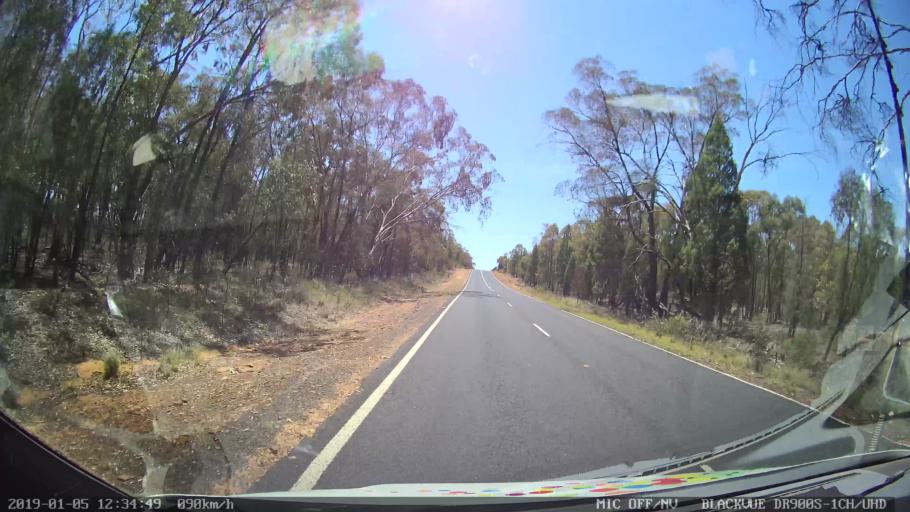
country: AU
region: New South Wales
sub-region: Warrumbungle Shire
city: Coonabarabran
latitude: -31.2112
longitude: 149.4163
